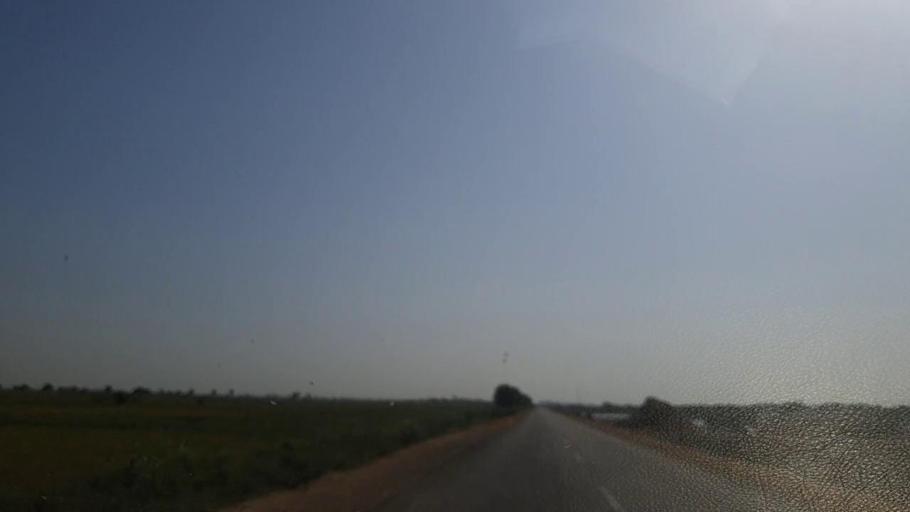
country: PK
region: Sindh
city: Jati
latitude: 24.5359
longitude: 68.2789
